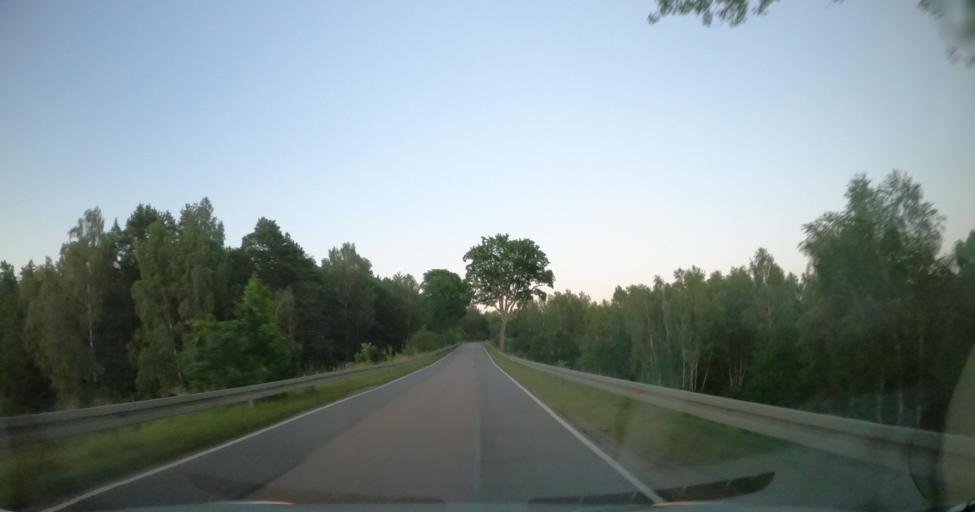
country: PL
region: Pomeranian Voivodeship
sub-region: Powiat wejherowski
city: Szemud
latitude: 54.4647
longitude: 18.1232
